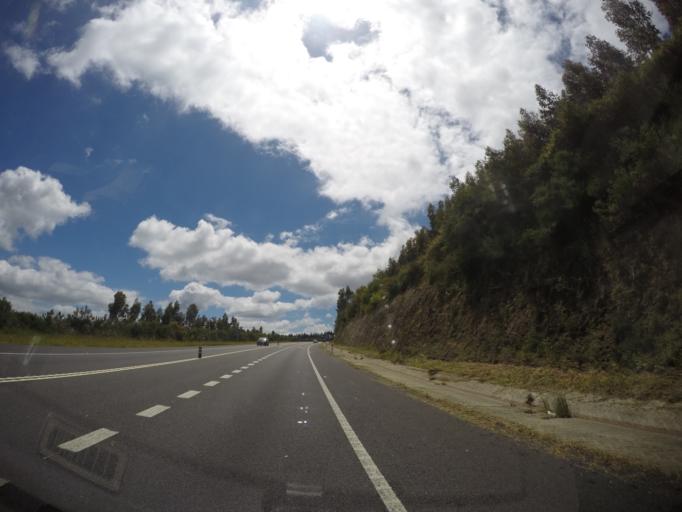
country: ES
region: Aragon
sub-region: Provincia de Zaragoza
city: Fuentes de Ebro
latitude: 41.5145
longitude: -0.6959
